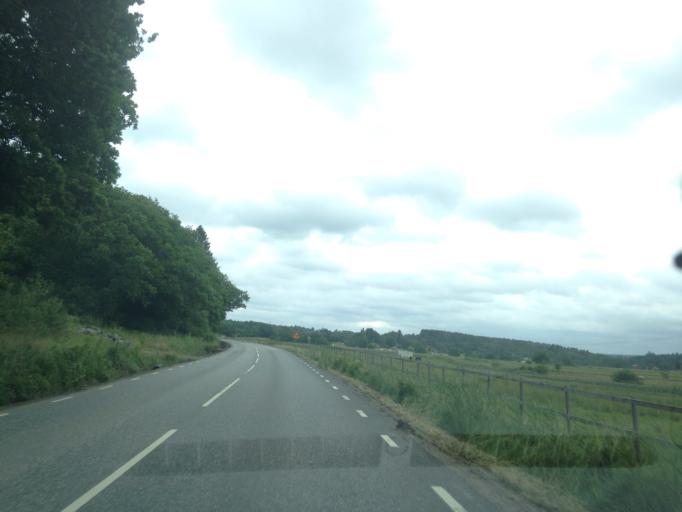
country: SE
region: Vaestra Goetaland
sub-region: Kungalvs Kommun
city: Kode
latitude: 57.8561
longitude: 11.8700
